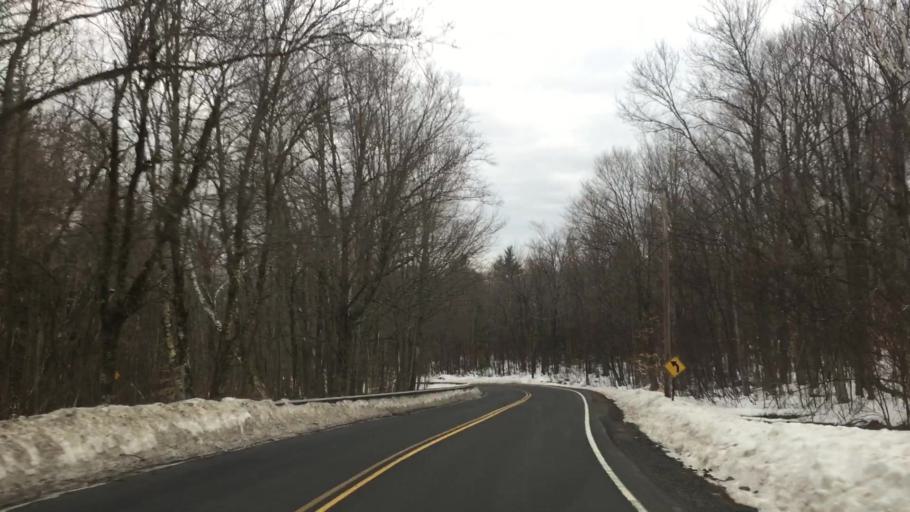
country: US
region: Massachusetts
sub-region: Berkshire County
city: Hinsdale
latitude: 42.4127
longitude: -73.0643
